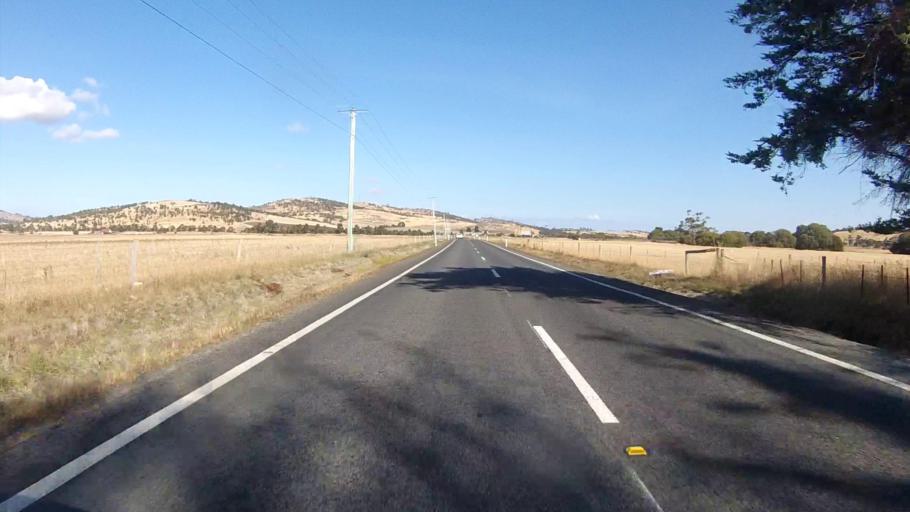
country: AU
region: Tasmania
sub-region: Sorell
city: Sorell
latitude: -42.7444
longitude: 147.5350
